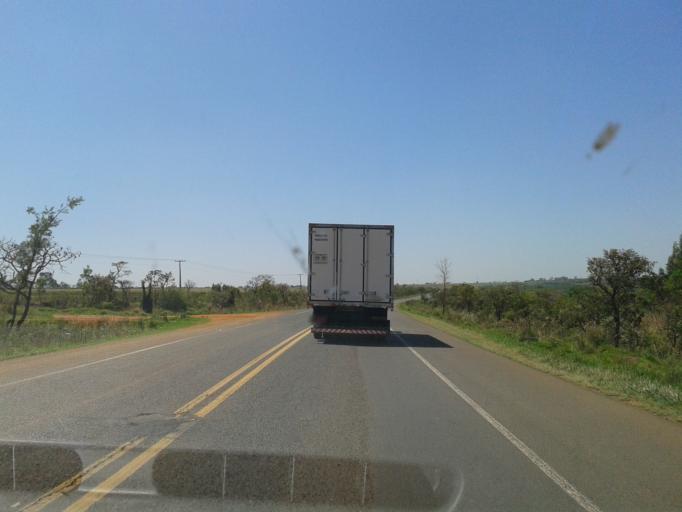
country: BR
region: Minas Gerais
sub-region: Patrocinio
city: Patrocinio
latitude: -19.2808
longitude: -47.4257
